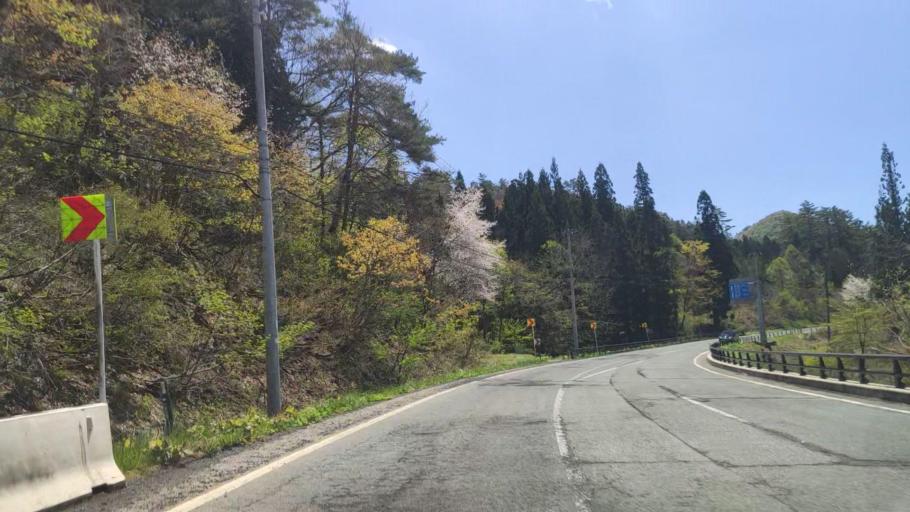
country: JP
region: Yamagata
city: Shinjo
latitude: 38.9157
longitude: 140.3255
